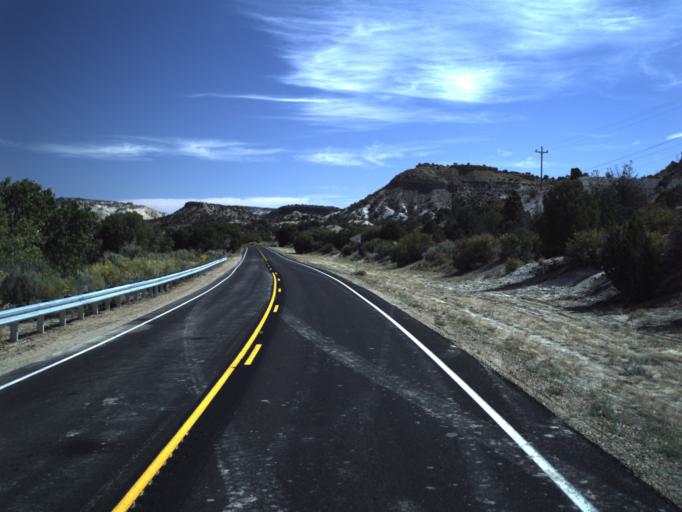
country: US
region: Utah
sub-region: Wayne County
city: Loa
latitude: 37.7721
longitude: -111.6552
